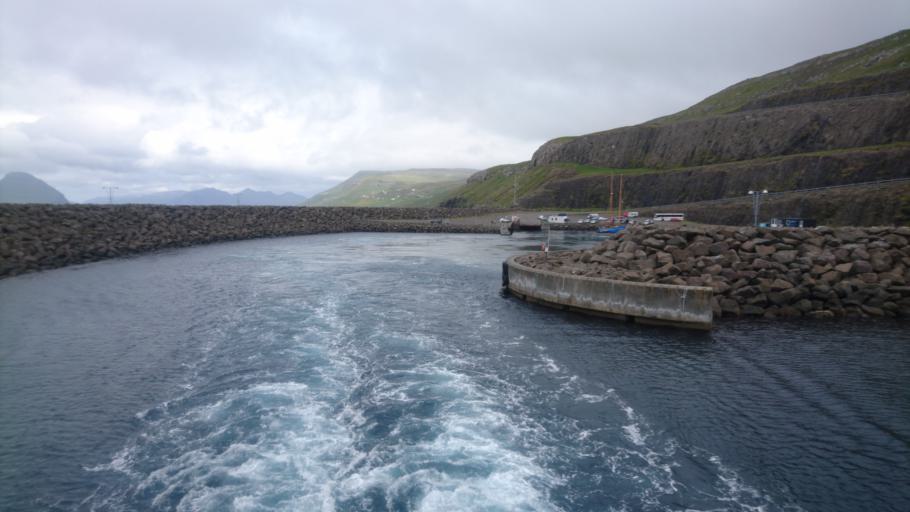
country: FO
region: Streymoy
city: Argir
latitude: 61.9605
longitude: -6.8171
